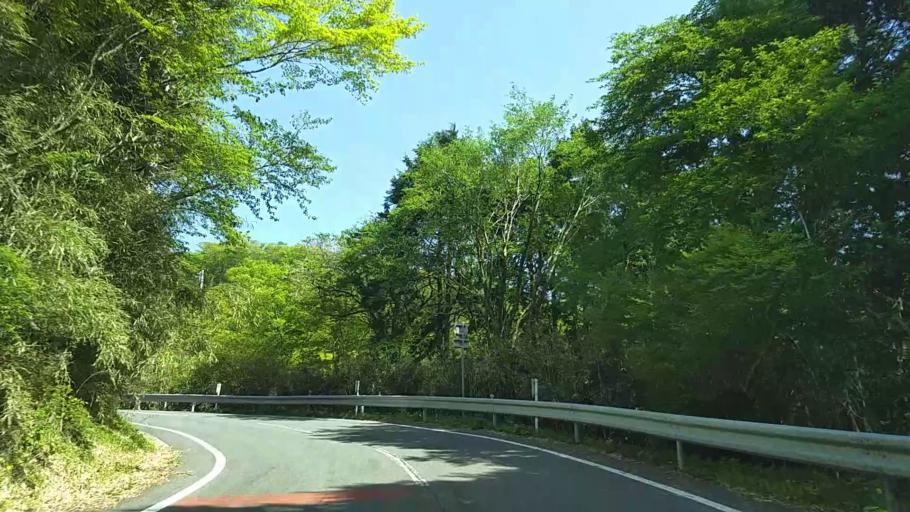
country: JP
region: Shizuoka
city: Gotemba
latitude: 35.2646
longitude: 138.9665
